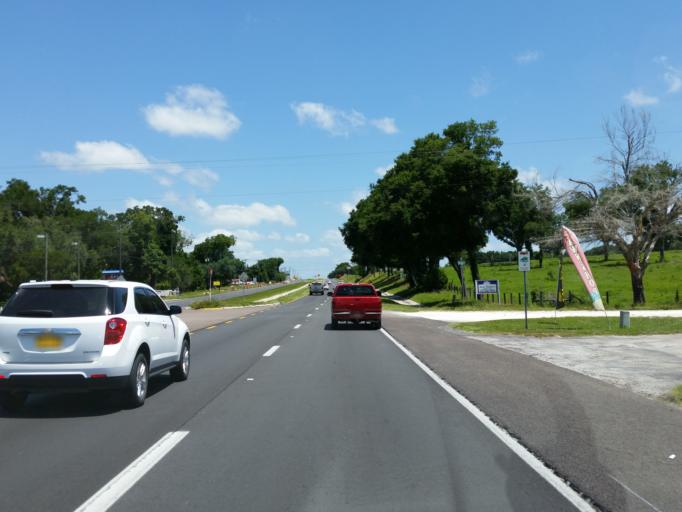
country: US
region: Florida
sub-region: Pasco County
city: Zephyrhills North
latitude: 28.3061
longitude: -82.1876
